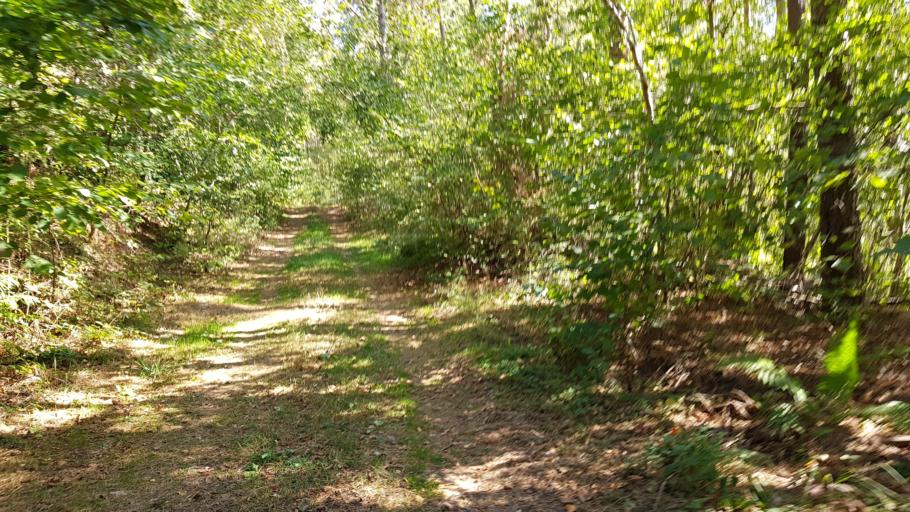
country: DE
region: Saxony
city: Grossnaundorf
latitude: 51.2183
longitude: 13.9506
